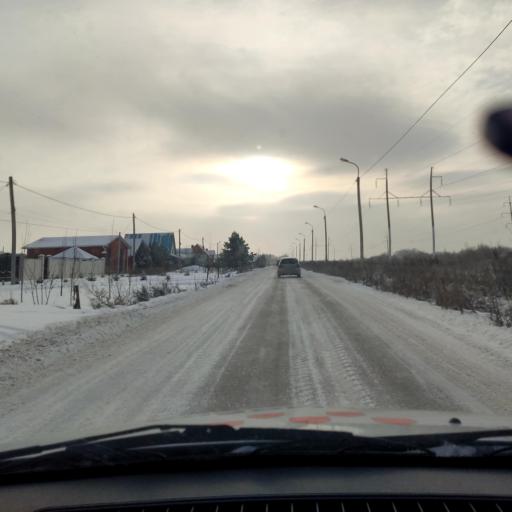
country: RU
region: Bashkortostan
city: Kabakovo
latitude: 54.6091
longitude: 56.0860
